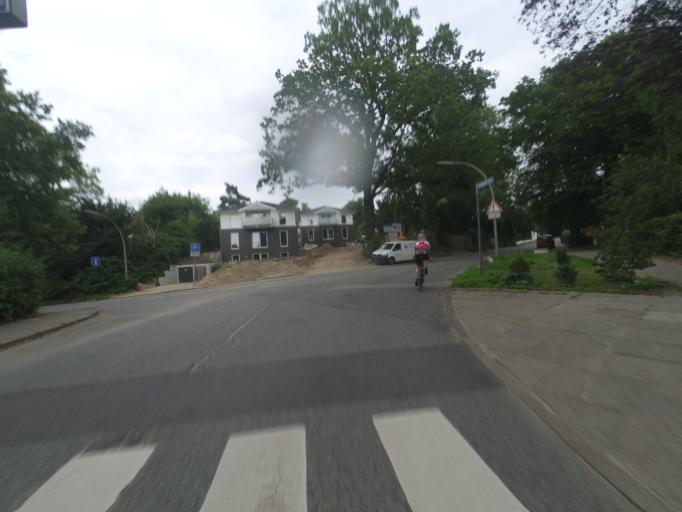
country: DE
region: Schleswig-Holstein
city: Oststeinbek
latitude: 53.5122
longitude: 10.1609
